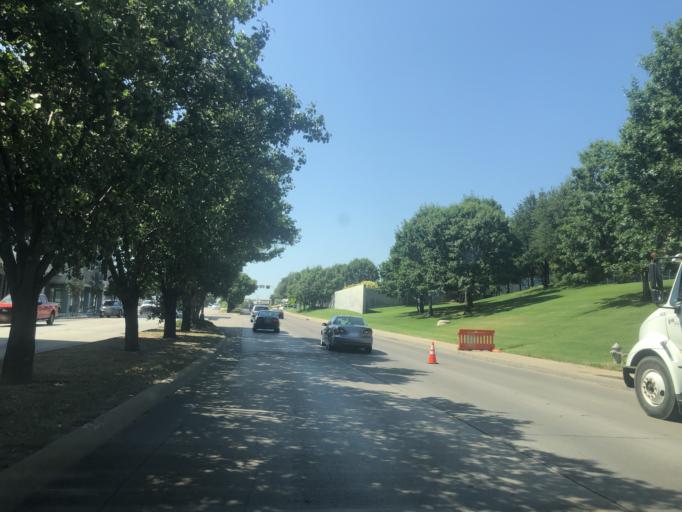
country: US
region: Texas
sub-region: Tarrant County
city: River Oaks
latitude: 32.7501
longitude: -97.3619
